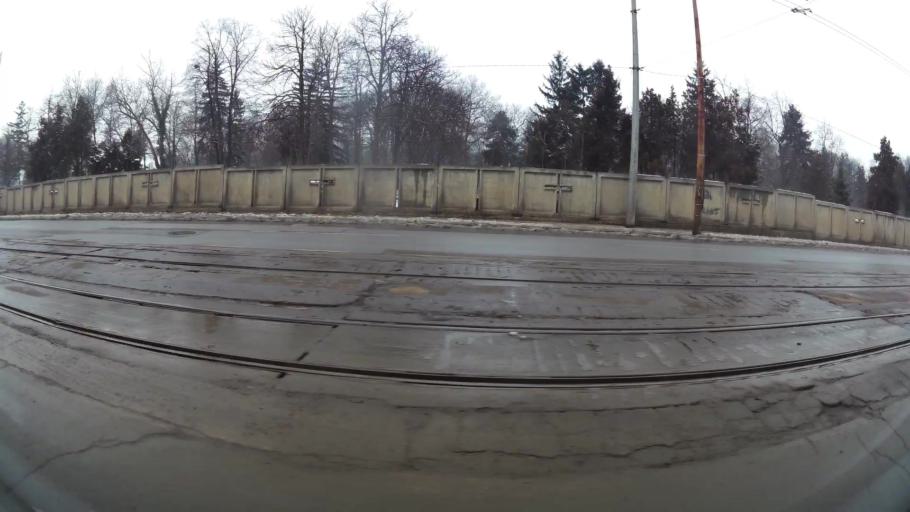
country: BG
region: Sofia-Capital
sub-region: Stolichna Obshtina
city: Sofia
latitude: 42.7122
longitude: 23.3376
